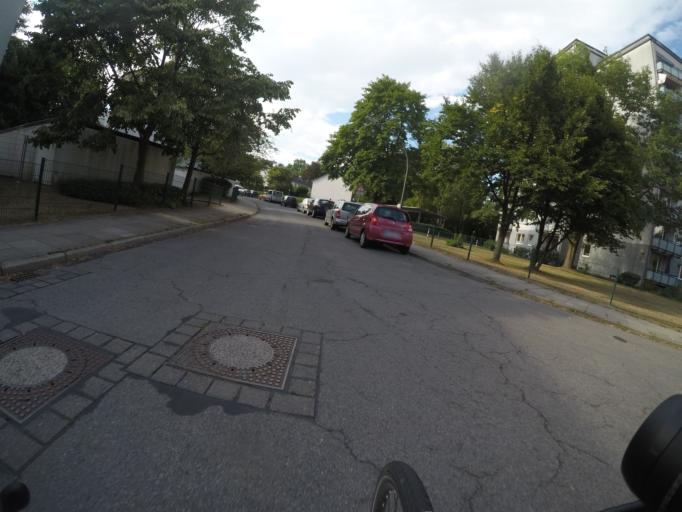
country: DE
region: Schleswig-Holstein
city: Glinde
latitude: 53.5059
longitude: 10.1891
